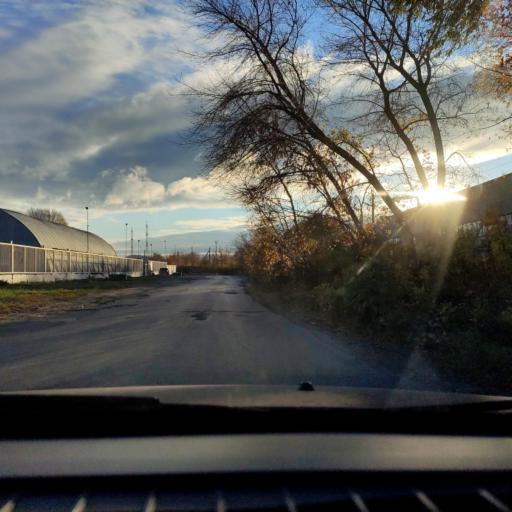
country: RU
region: Samara
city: Tol'yatti
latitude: 53.5752
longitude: 49.2861
